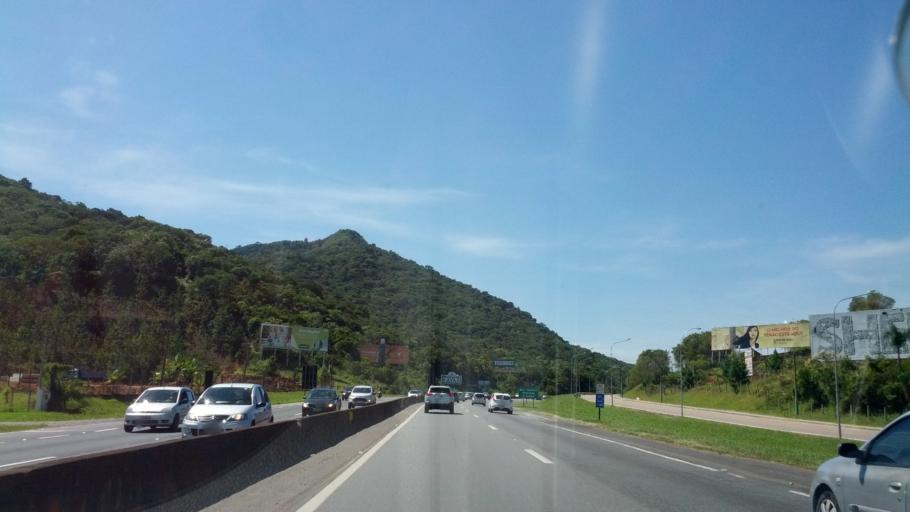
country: BR
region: Santa Catarina
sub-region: Balneario Camboriu
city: Balneario Camboriu
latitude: -26.9838
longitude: -48.6704
